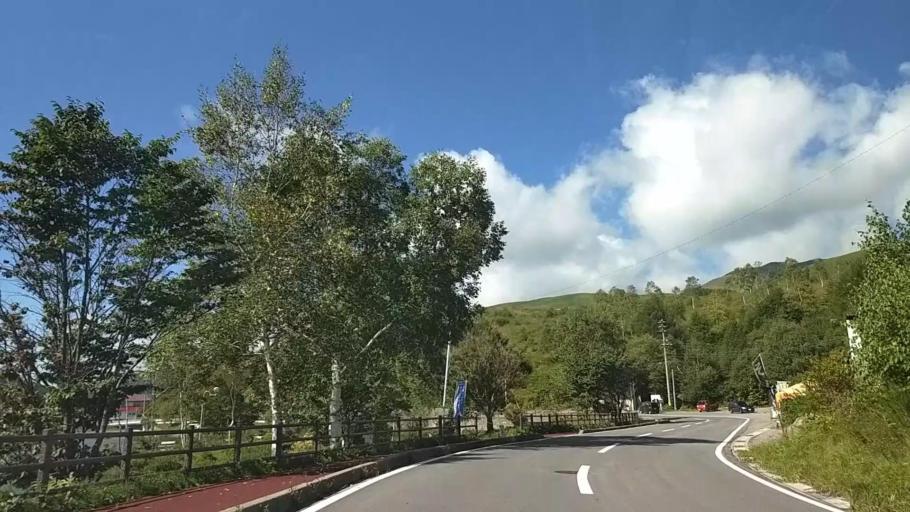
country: JP
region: Nagano
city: Chino
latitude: 36.1038
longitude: 138.2306
